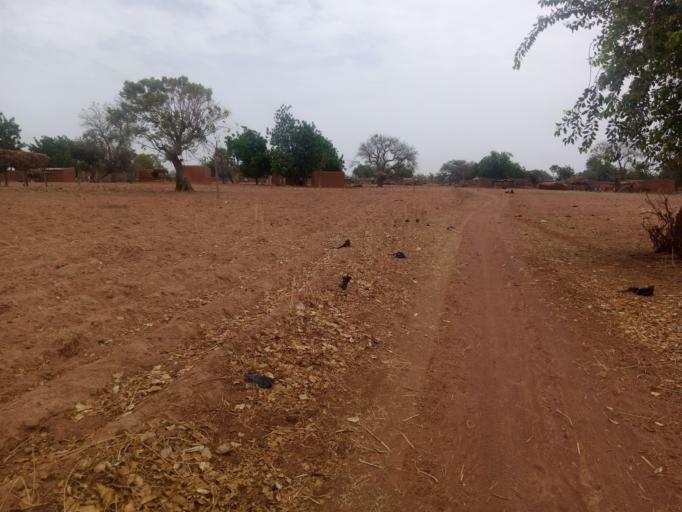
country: BF
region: Boucle du Mouhoun
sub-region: Province de la Kossi
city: Nouna
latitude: 12.8535
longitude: -4.0758
